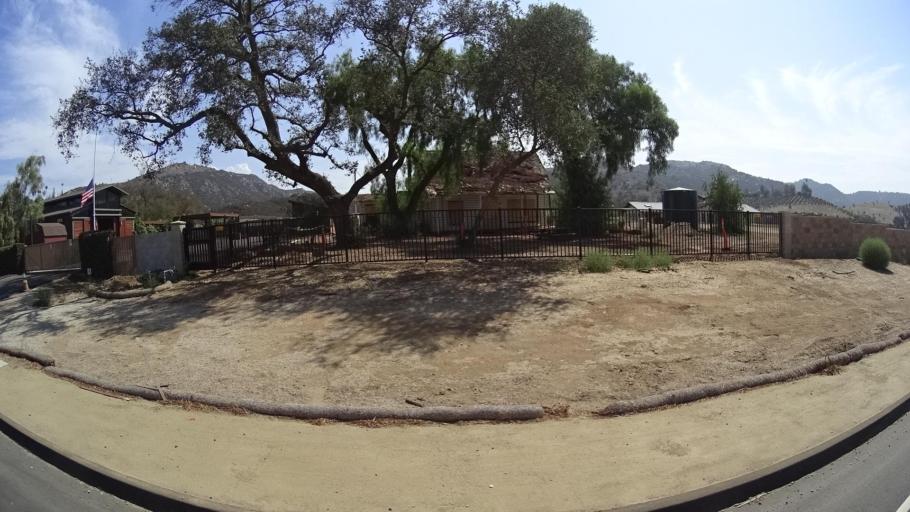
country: US
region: California
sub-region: San Diego County
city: San Marcos
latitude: 33.1919
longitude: -117.1516
